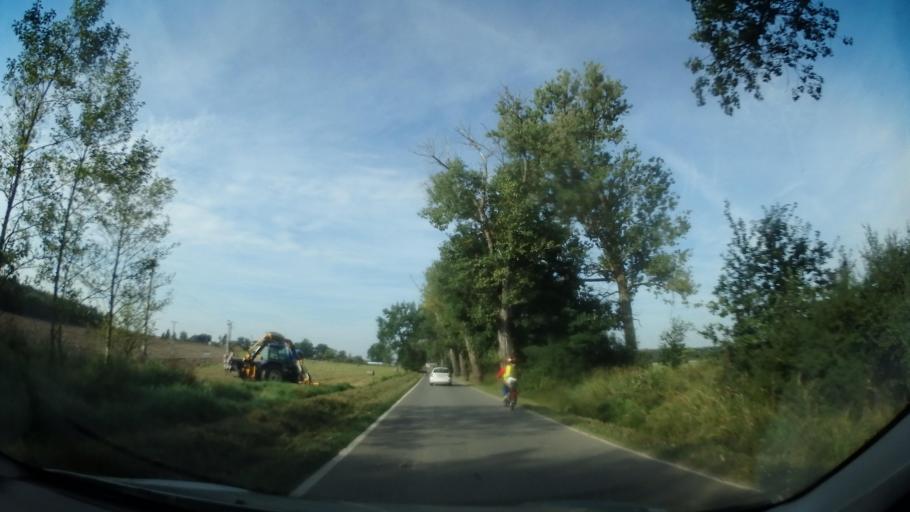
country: CZ
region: Jihocesky
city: Cimelice
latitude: 49.4294
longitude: 14.1251
